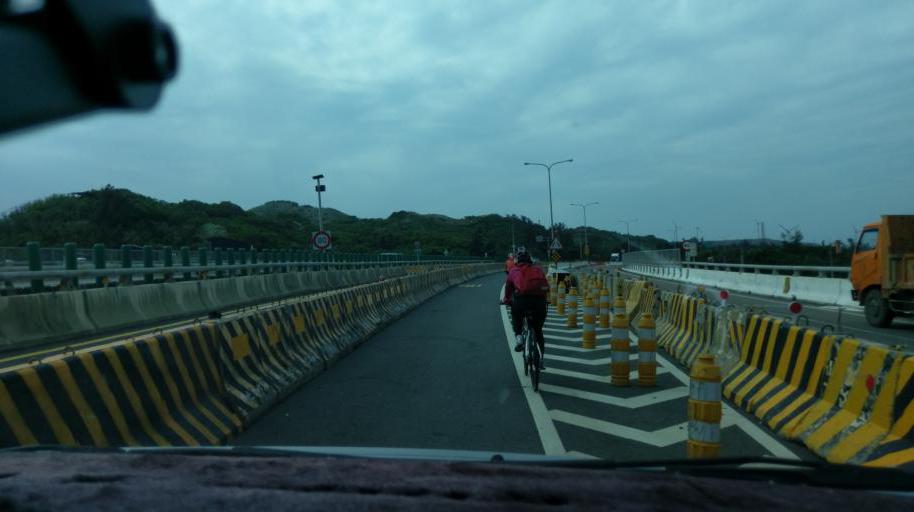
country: TW
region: Taiwan
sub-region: Miaoli
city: Miaoli
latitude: 24.6116
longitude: 120.7610
